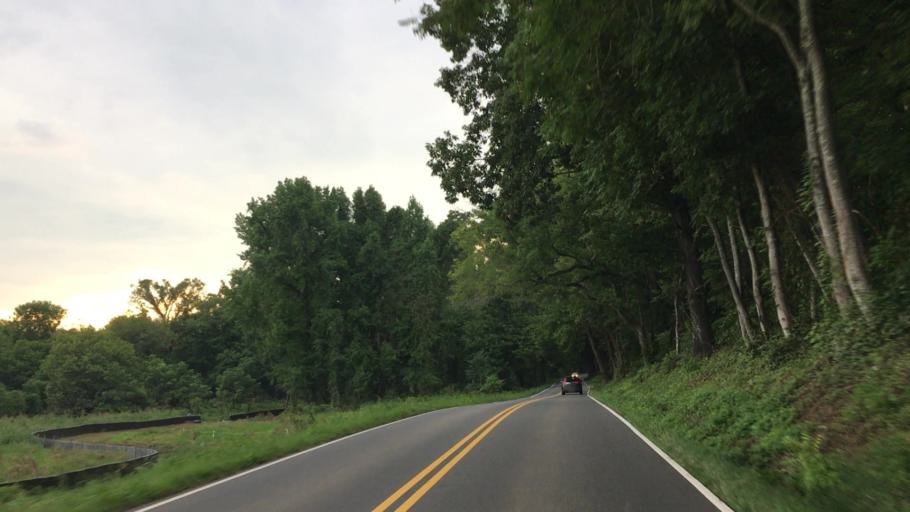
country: US
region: Virginia
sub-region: City of Fredericksburg
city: Fredericksburg
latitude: 38.3087
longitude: -77.4579
